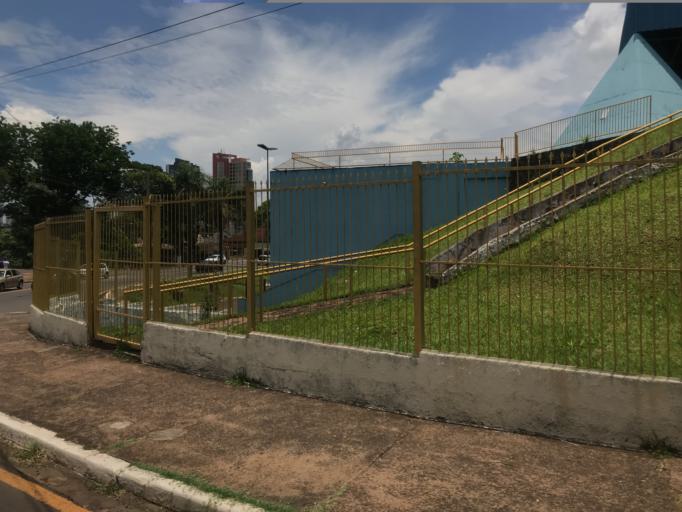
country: BR
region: Parana
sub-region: Londrina
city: Londrina
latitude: -23.3216
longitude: -51.1634
